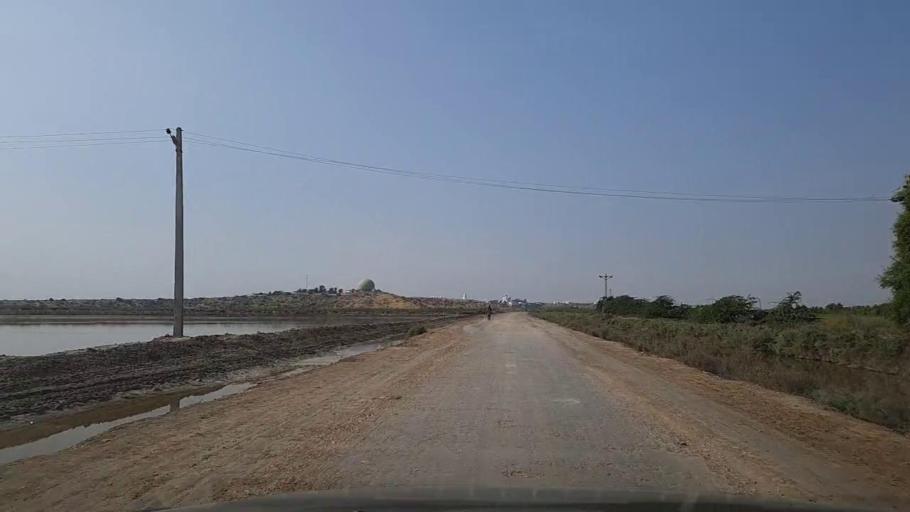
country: PK
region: Sindh
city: Chuhar Jamali
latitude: 24.5499
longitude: 67.8956
